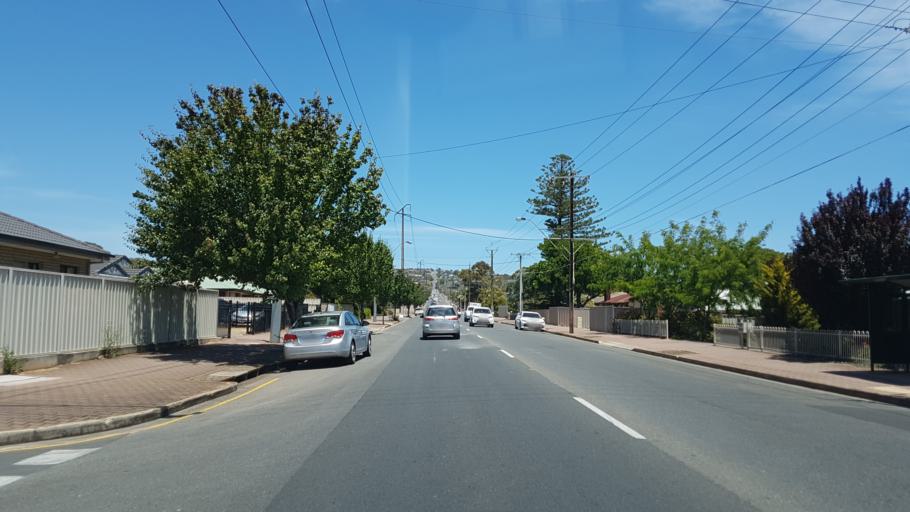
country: AU
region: South Australia
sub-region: Marion
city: Sturt
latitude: -35.0223
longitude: 138.5413
